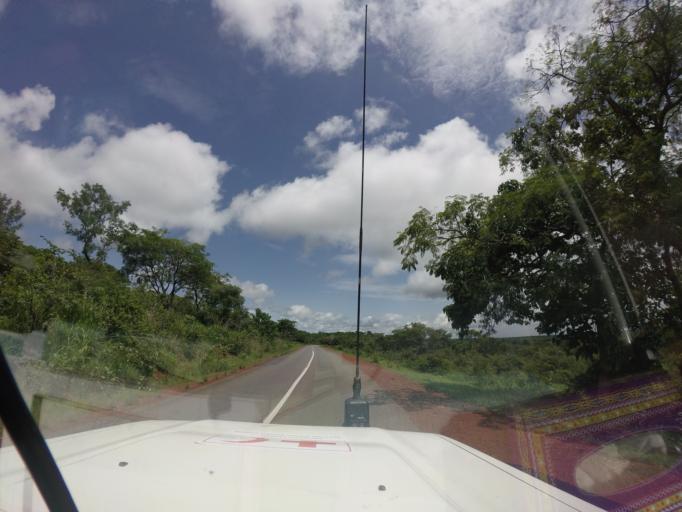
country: GN
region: Faranah
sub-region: Faranah Prefecture
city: Faranah
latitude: 10.0233
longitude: -10.8052
